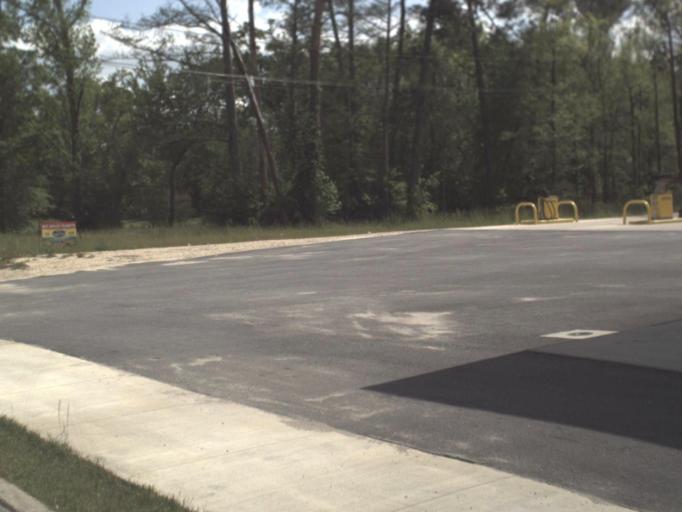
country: US
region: Alabama
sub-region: Escambia County
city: Flomaton
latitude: 30.9947
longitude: -87.2586
